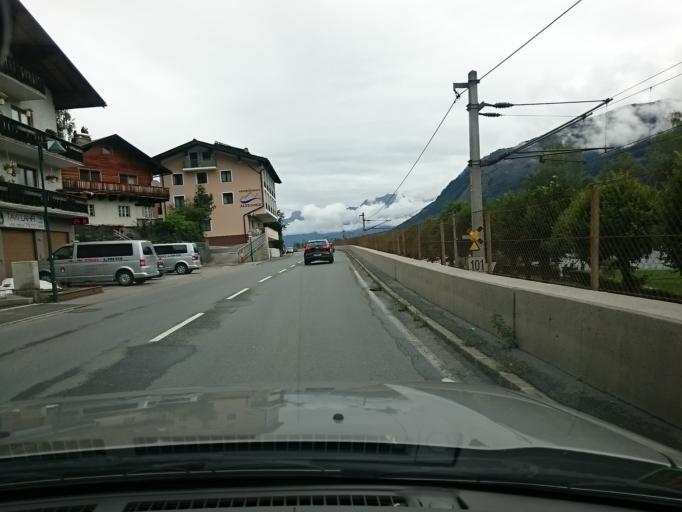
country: AT
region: Salzburg
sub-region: Politischer Bezirk Zell am See
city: Zell am See
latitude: 47.3332
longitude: 12.7970
